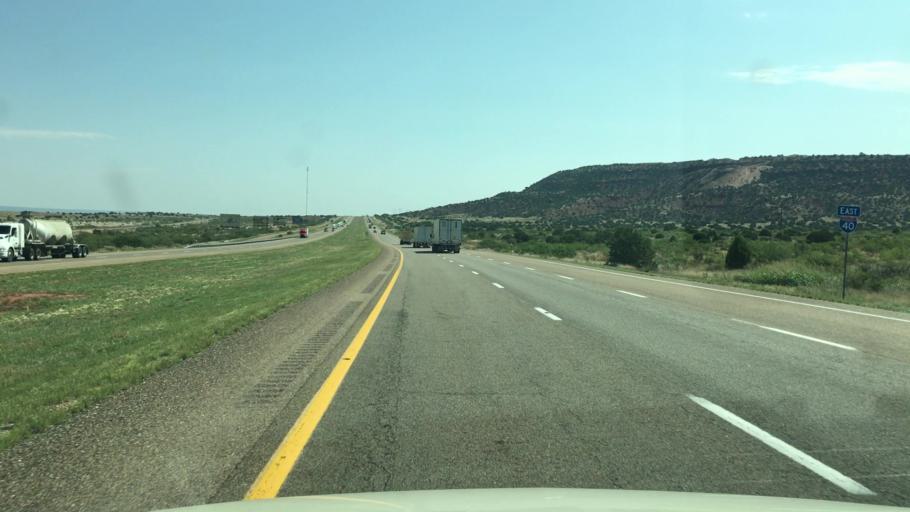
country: US
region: New Mexico
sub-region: Guadalupe County
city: Santa Rosa
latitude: 35.0360
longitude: -104.3982
